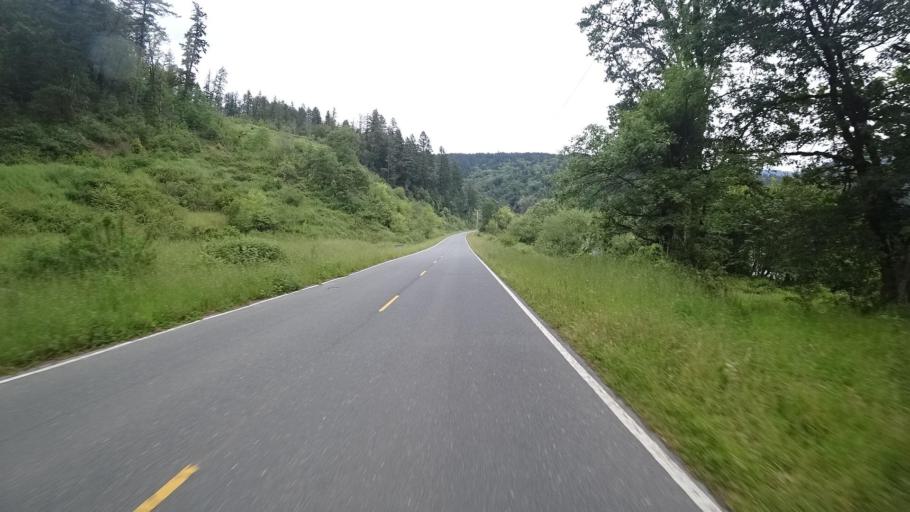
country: US
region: California
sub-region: Humboldt County
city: Willow Creek
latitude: 41.0957
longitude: -123.7116
